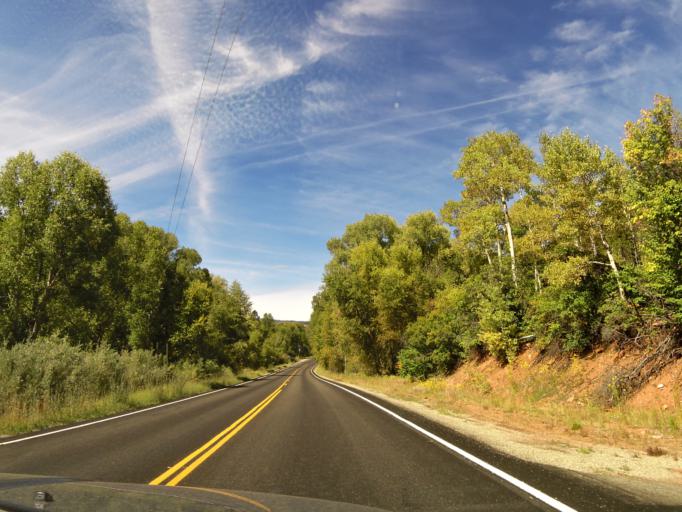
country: US
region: Colorado
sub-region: Montezuma County
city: Mancos
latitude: 37.5790
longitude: -108.2130
